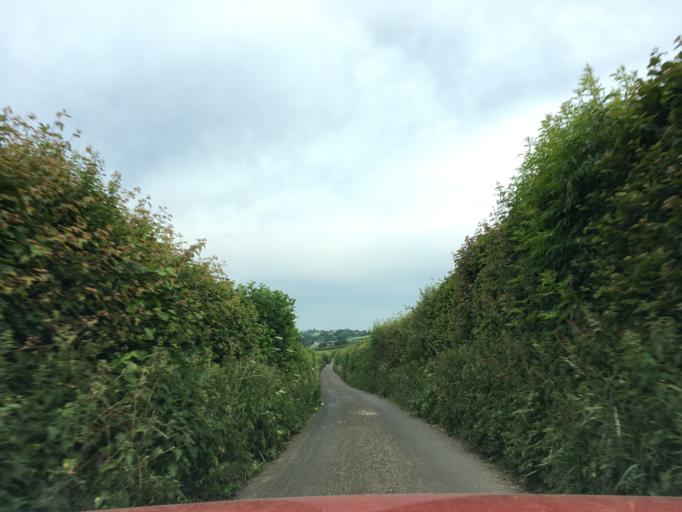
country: GB
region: England
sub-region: Bath and North East Somerset
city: Stanton Drew
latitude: 51.3936
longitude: -2.5977
